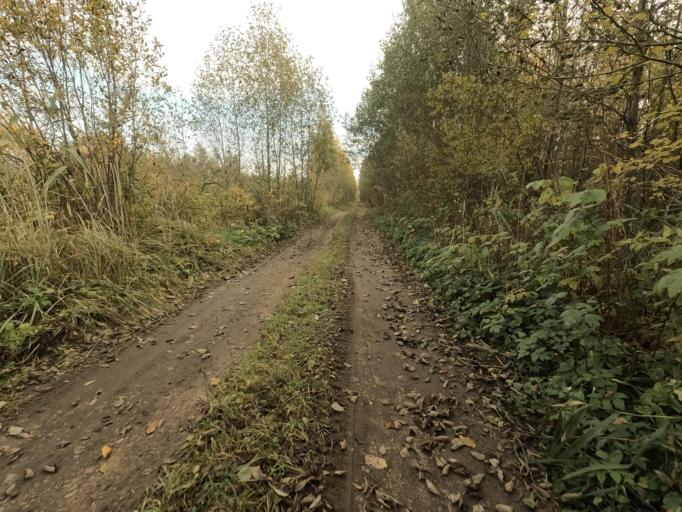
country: RU
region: Novgorod
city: Pankovka
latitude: 58.8792
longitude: 30.8535
